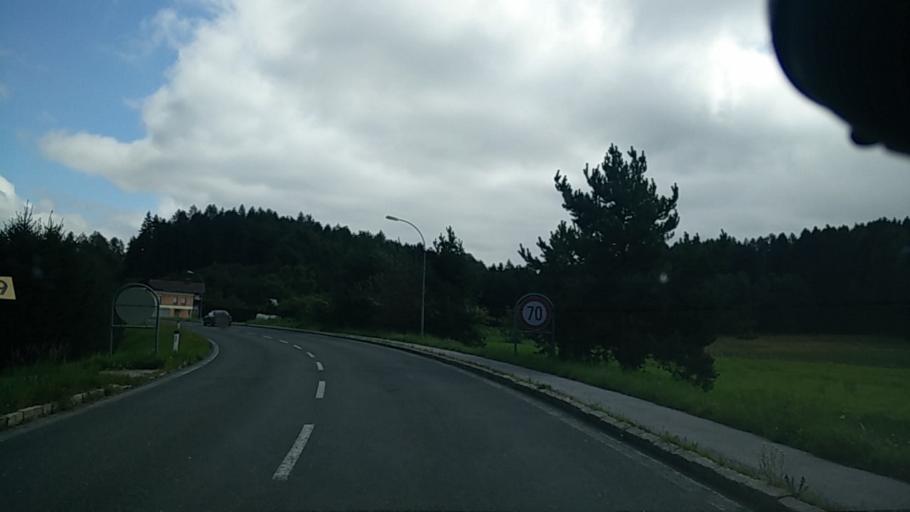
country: AT
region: Carinthia
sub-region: Politischer Bezirk Villach Land
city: Wernberg
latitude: 46.5566
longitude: 13.9306
